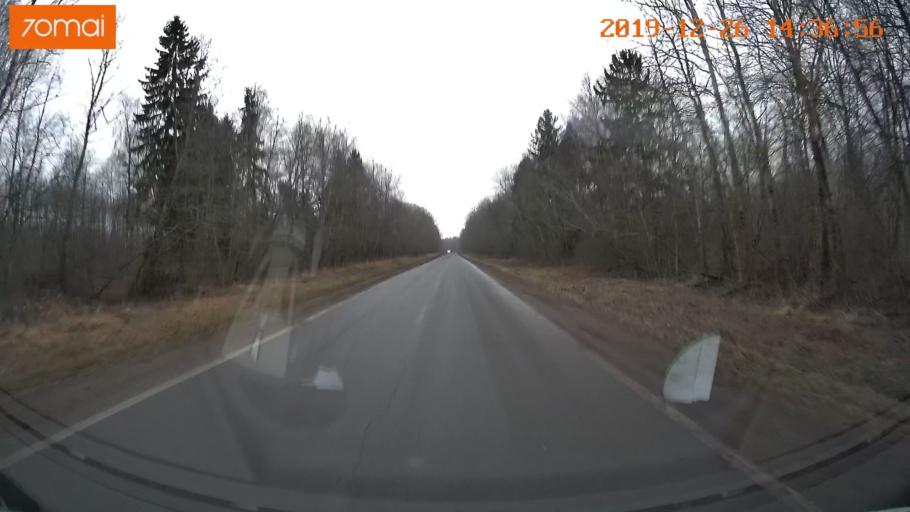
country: RU
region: Jaroslavl
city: Poshekhon'ye
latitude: 58.4069
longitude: 38.9743
